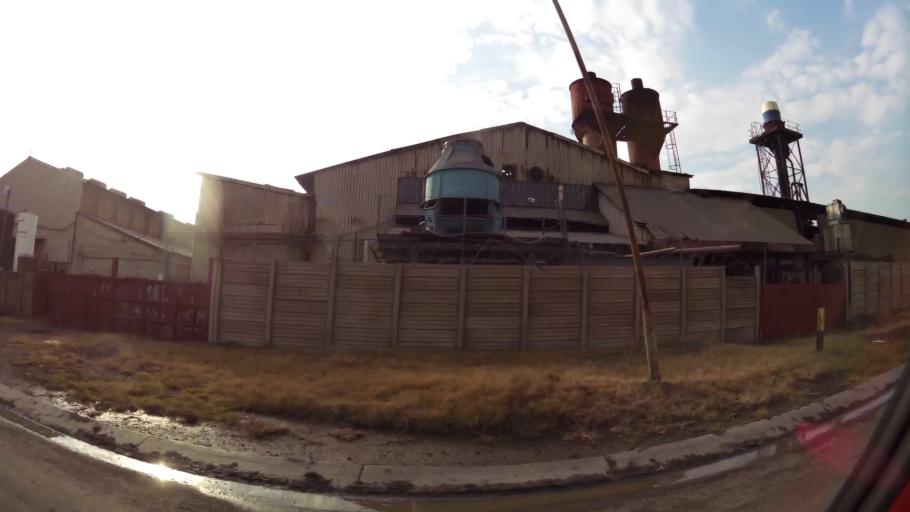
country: ZA
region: Gauteng
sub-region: Sedibeng District Municipality
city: Vereeniging
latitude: -26.6815
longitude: 27.9089
